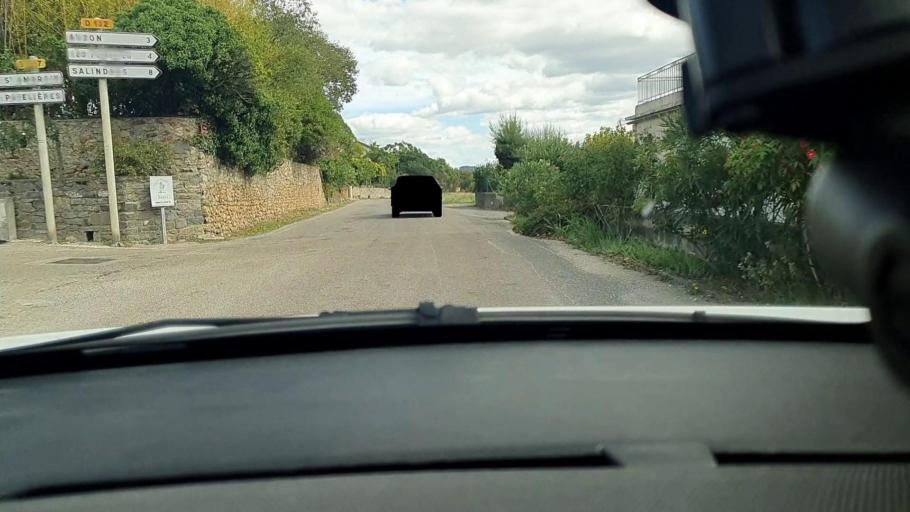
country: FR
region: Languedoc-Roussillon
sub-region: Departement du Gard
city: Les Mages
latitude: 44.2116
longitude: 4.1973
